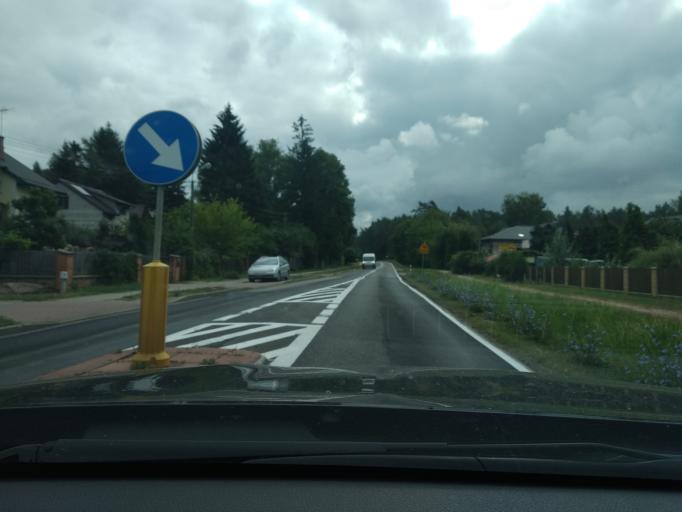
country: PL
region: Masovian Voivodeship
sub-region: Powiat pultuski
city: Obryte
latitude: 52.6468
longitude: 21.2533
